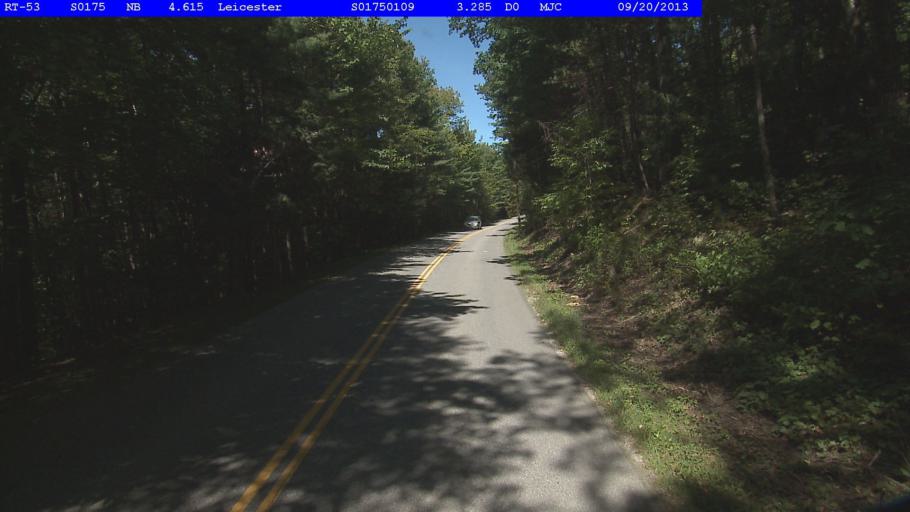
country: US
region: Vermont
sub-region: Rutland County
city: Brandon
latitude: 43.8898
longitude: -73.0649
